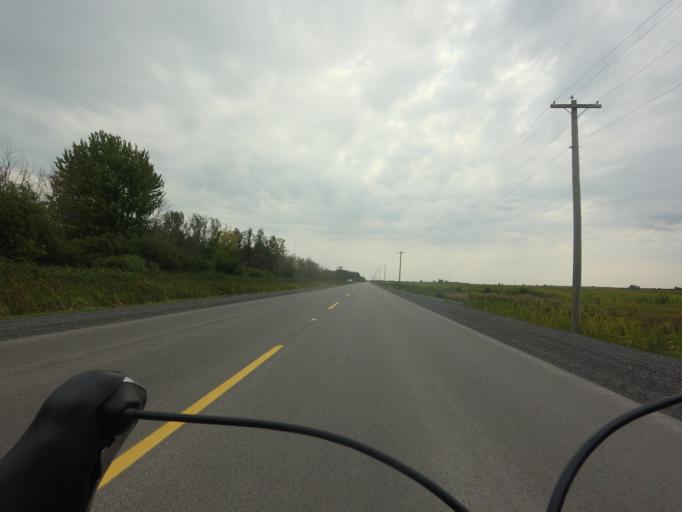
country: CA
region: Ontario
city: Bells Corners
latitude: 45.2195
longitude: -75.7737
